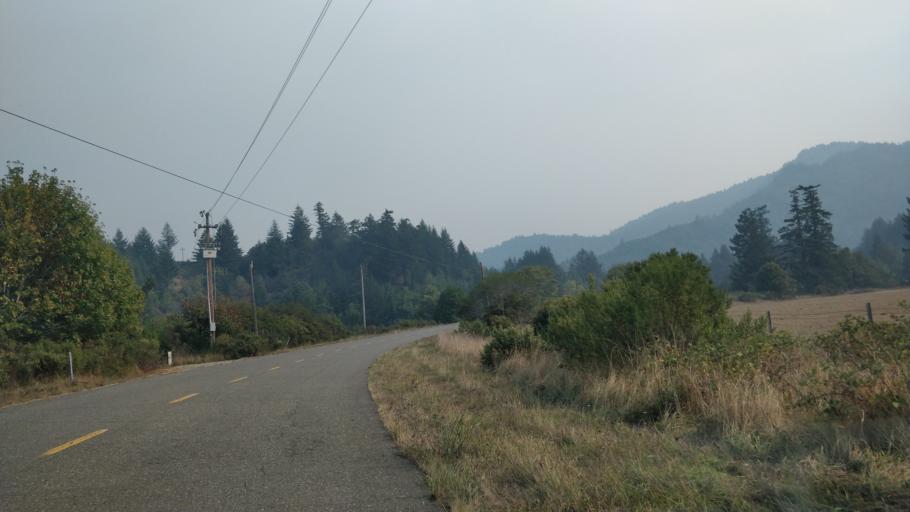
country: US
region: California
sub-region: Humboldt County
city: Rio Dell
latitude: 40.2787
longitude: -124.2447
